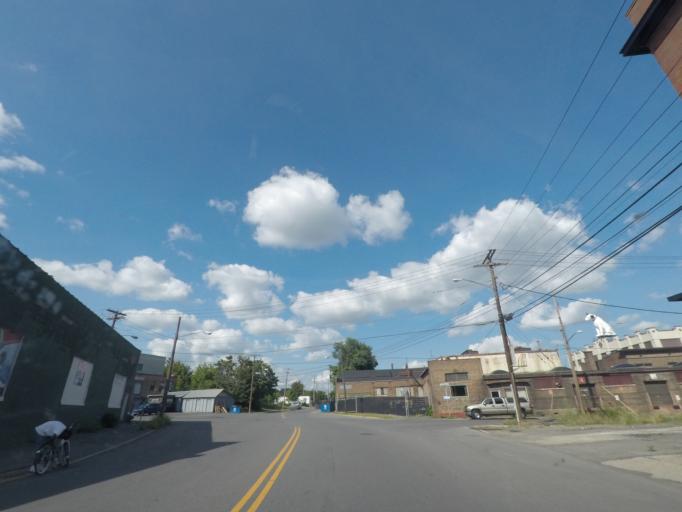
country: US
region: New York
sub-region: Albany County
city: Albany
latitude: 42.6635
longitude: -73.7442
